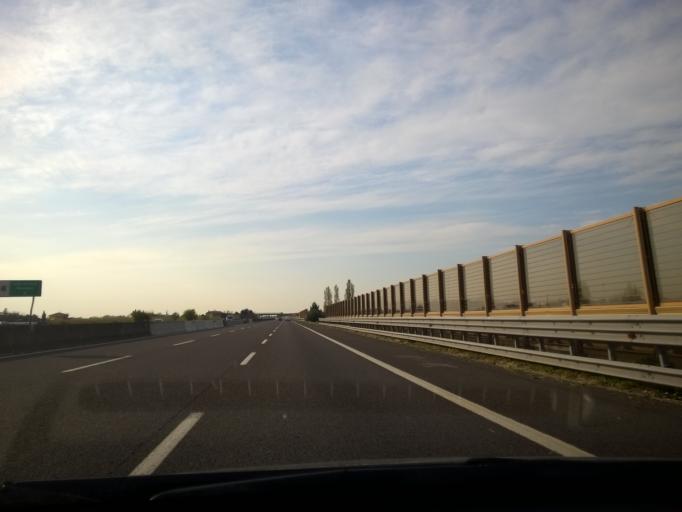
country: IT
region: Emilia-Romagna
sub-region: Forli-Cesena
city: Cesena
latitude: 44.1778
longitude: 12.2665
